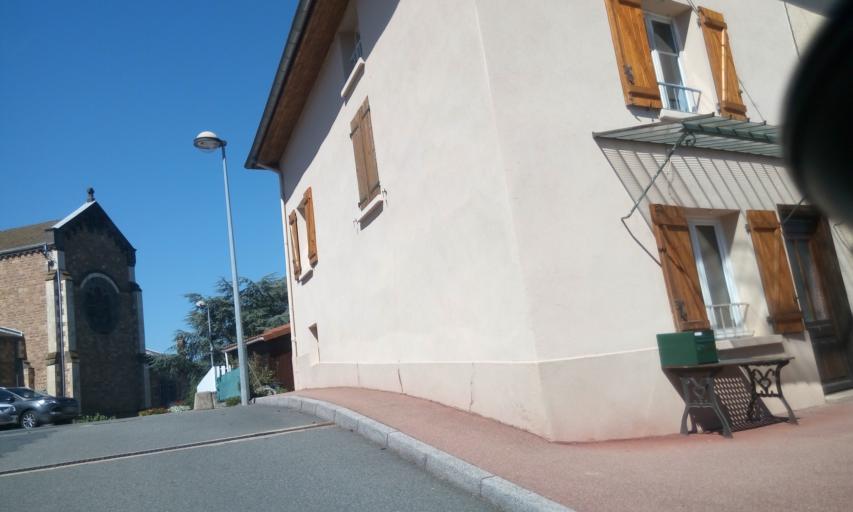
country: FR
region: Rhone-Alpes
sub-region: Departement du Rhone
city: Grandris
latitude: 46.0021
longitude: 4.4483
